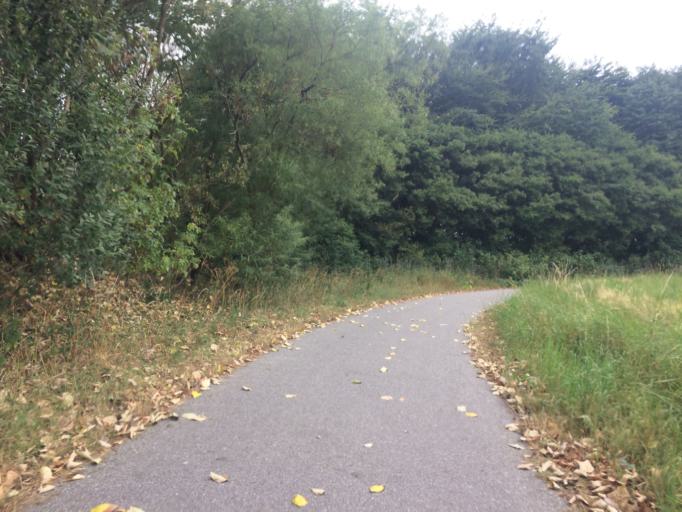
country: DK
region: Central Jutland
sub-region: Struer Kommune
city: Struer
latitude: 56.4769
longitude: 8.6130
